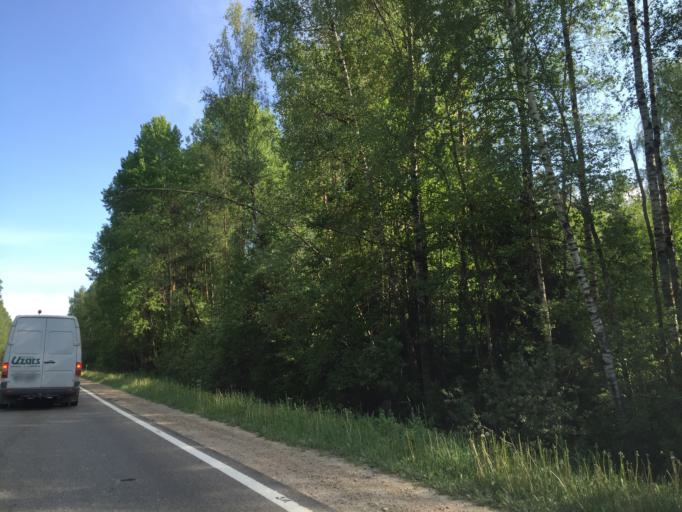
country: LV
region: Salaspils
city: Salaspils
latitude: 56.9159
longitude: 24.3998
